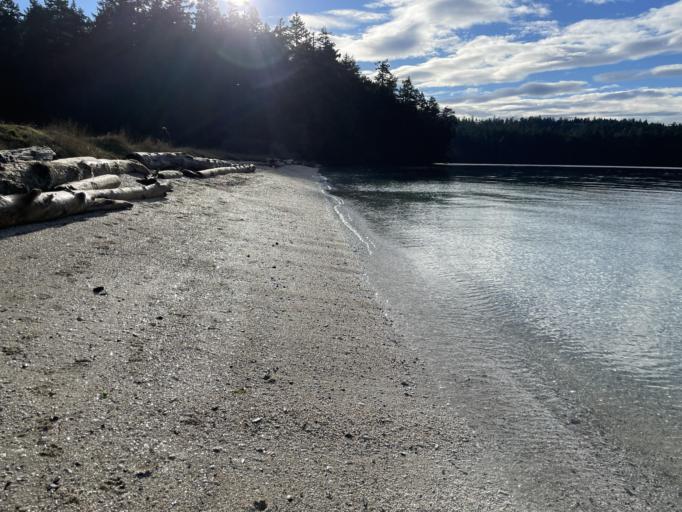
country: CA
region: British Columbia
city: North Saanich
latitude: 48.8989
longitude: -123.4078
